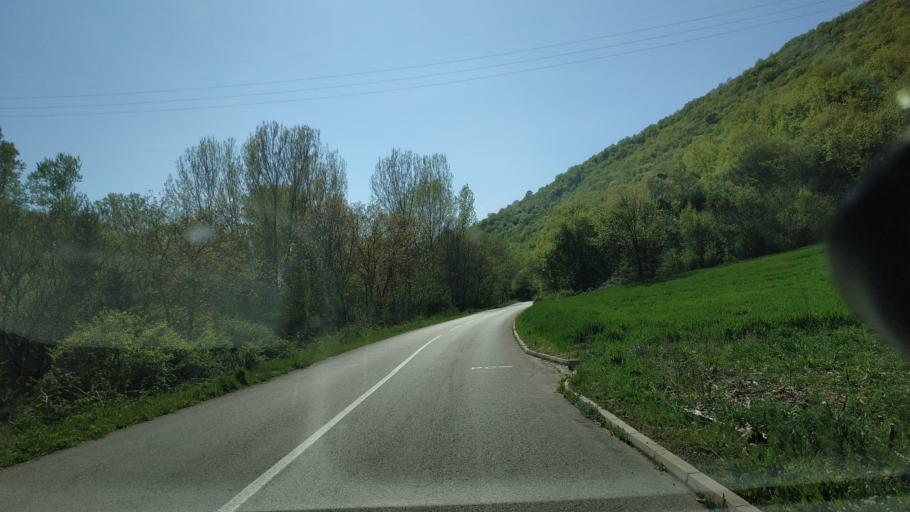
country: RS
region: Central Serbia
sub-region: Nisavski Okrug
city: Nis
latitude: 43.4183
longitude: 21.8439
